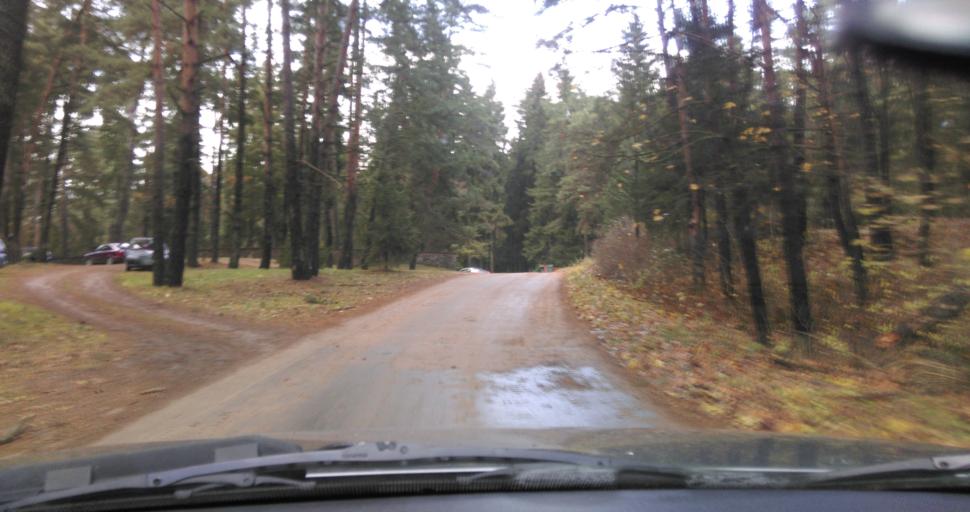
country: LT
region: Utenos apskritis
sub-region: Utena
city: Utena
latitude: 55.5904
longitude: 25.4979
